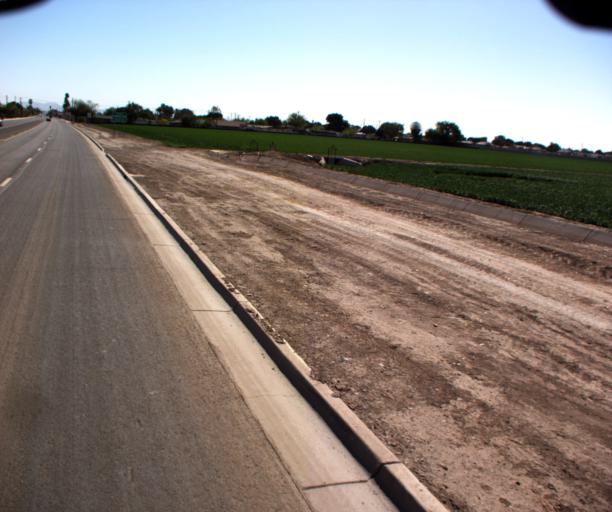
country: US
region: Arizona
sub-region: Yuma County
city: Somerton
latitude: 32.5966
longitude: -114.7232
